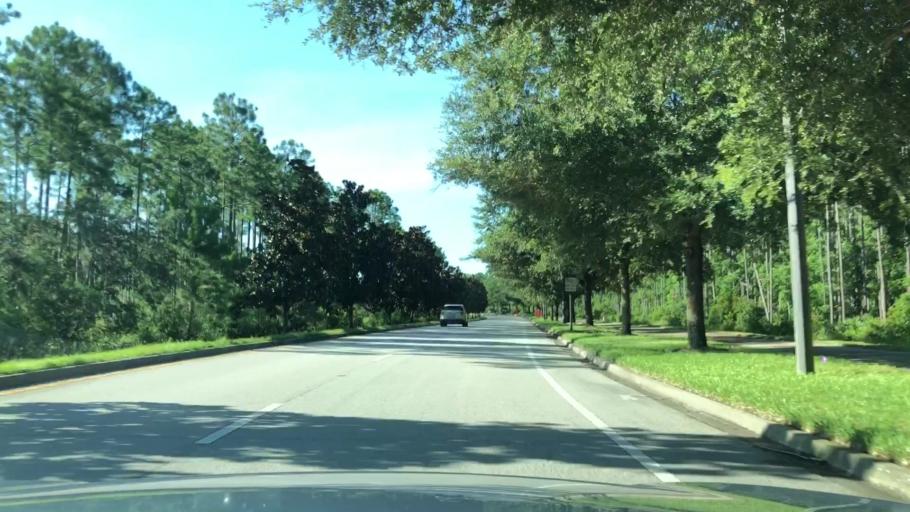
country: US
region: Florida
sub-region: Saint Johns County
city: Palm Valley
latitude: 30.0994
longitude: -81.4101
